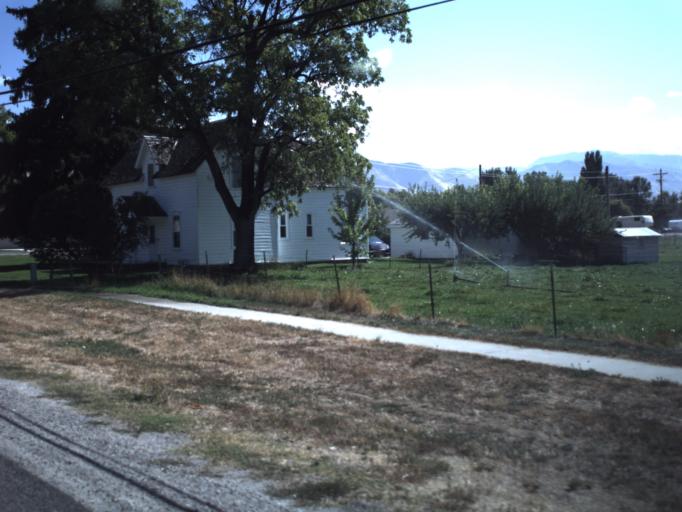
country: US
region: Utah
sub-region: Cache County
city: Smithfield
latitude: 41.8387
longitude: -111.8449
